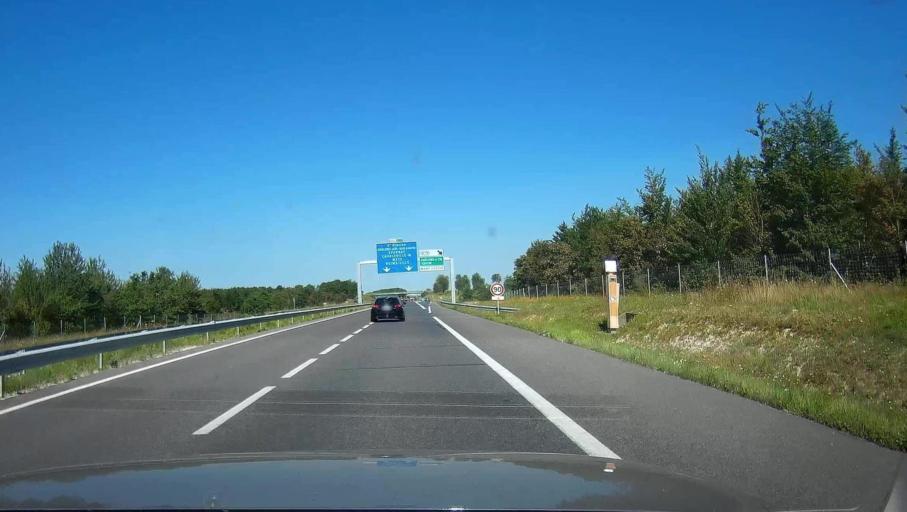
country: FR
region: Champagne-Ardenne
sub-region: Departement de la Marne
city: Fagnieres
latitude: 48.9026
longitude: 4.2852
